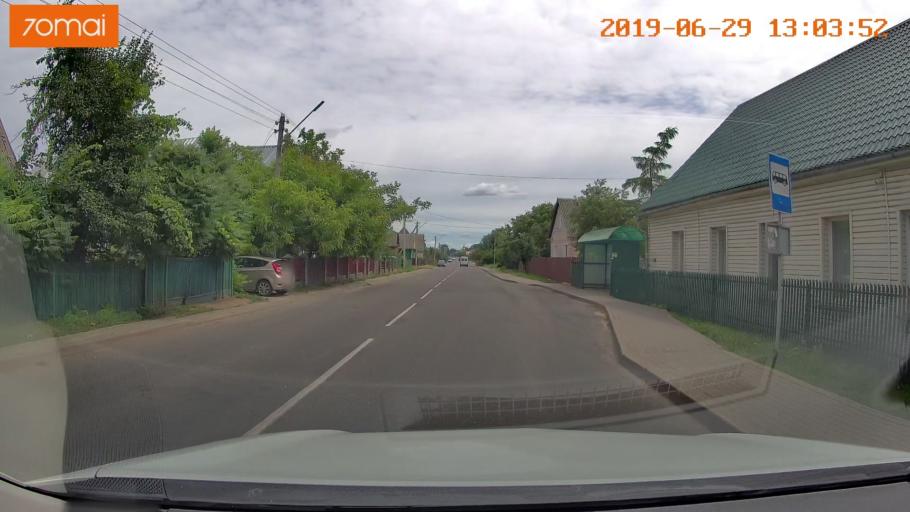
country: BY
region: Minsk
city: Slutsk
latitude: 53.0312
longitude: 27.5650
